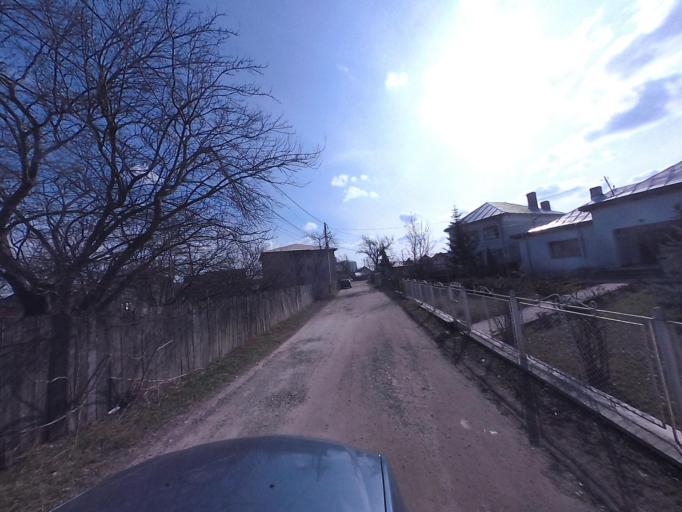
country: RO
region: Neamt
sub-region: Oras Targu Neamt
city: Targu Neamt
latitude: 47.2031
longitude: 26.3713
